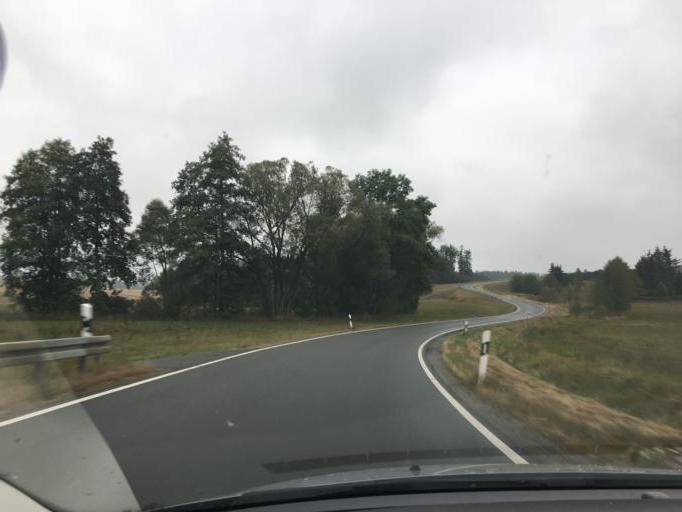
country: DE
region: Thuringia
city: Gorkwitz
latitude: 50.5654
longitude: 11.7580
